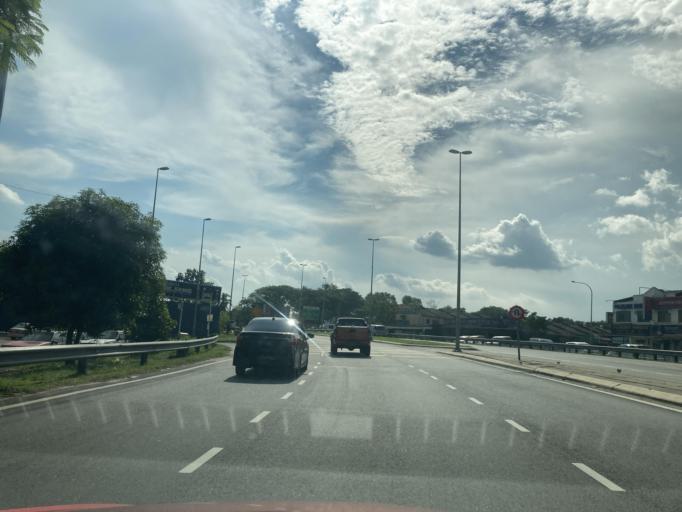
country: MY
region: Selangor
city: Kampung Baru Subang
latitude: 3.1501
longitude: 101.5427
